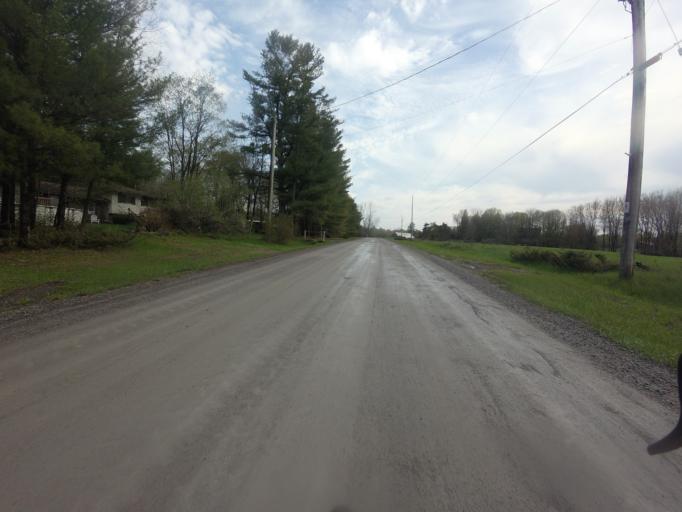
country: CA
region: Ontario
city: Carleton Place
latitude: 45.2029
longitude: -76.3229
